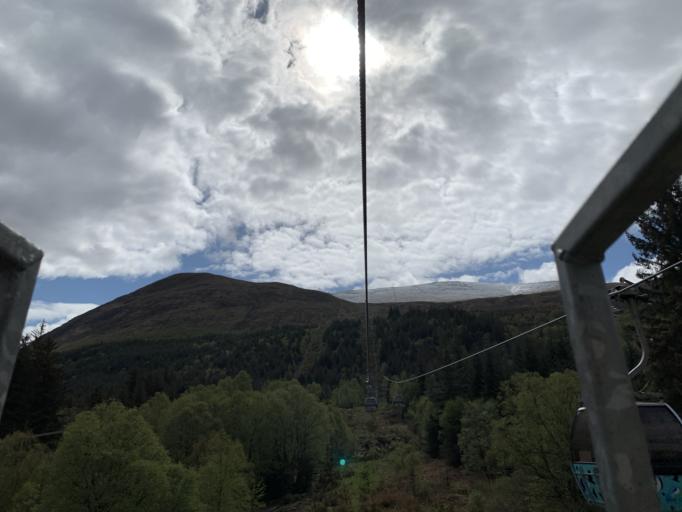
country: GB
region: Scotland
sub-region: Highland
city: Spean Bridge
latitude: 56.8477
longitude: -4.9911
